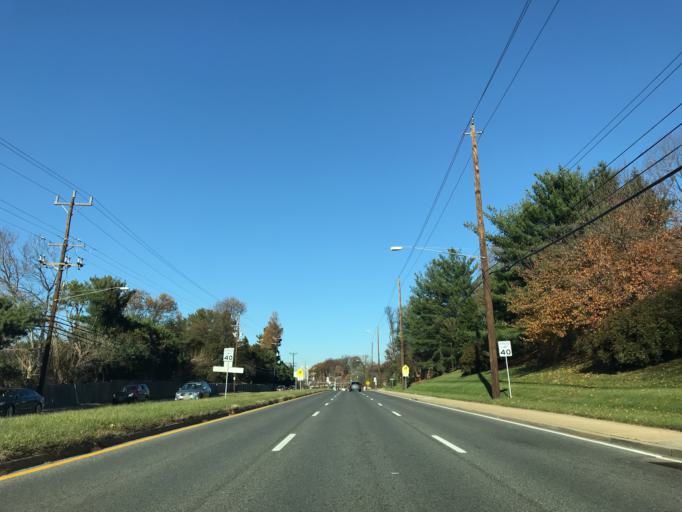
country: US
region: Maryland
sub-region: Montgomery County
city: North Bethesda
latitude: 39.0354
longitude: -77.1244
